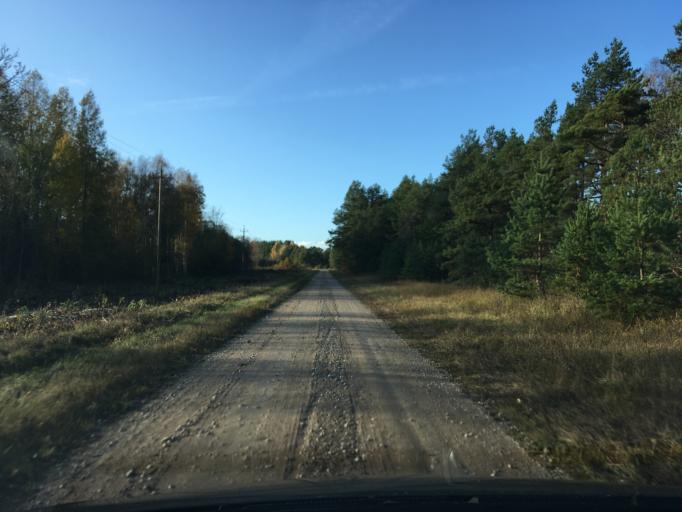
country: EE
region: Laeaene
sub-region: Lihula vald
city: Lihula
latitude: 58.5658
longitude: 23.7676
